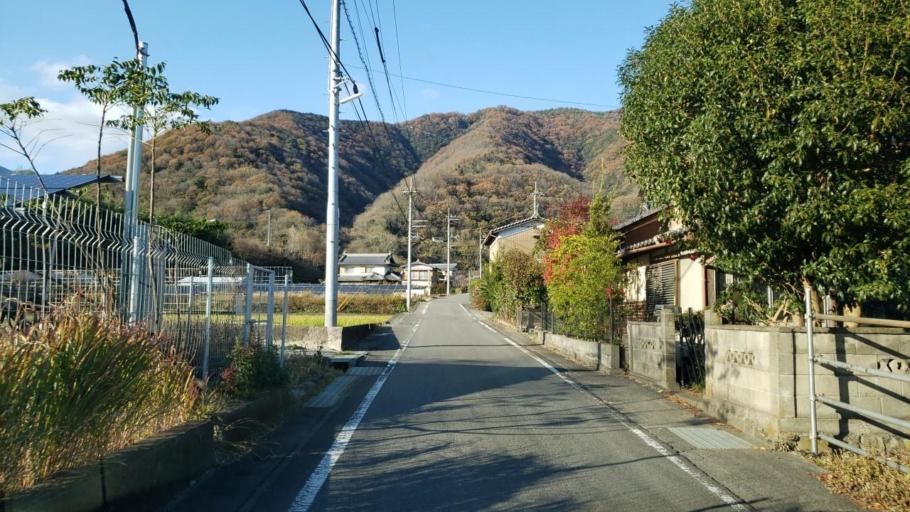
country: JP
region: Tokushima
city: Wakimachi
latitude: 34.0732
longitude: 134.0839
